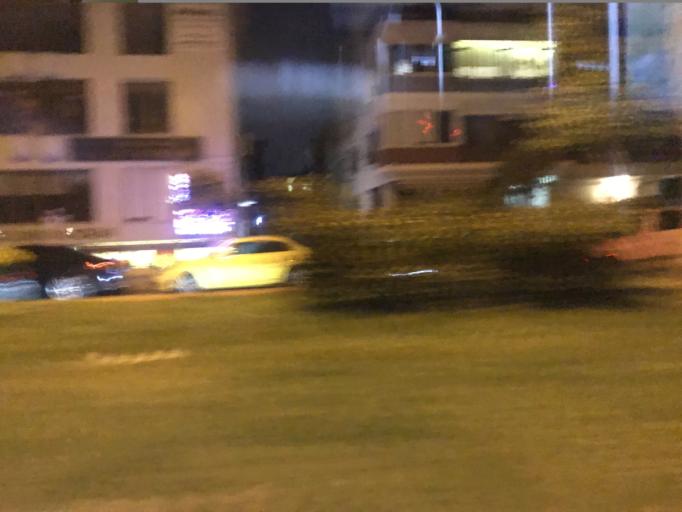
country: TR
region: Istanbul
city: Bahcelievler
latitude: 40.9633
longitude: 28.8395
